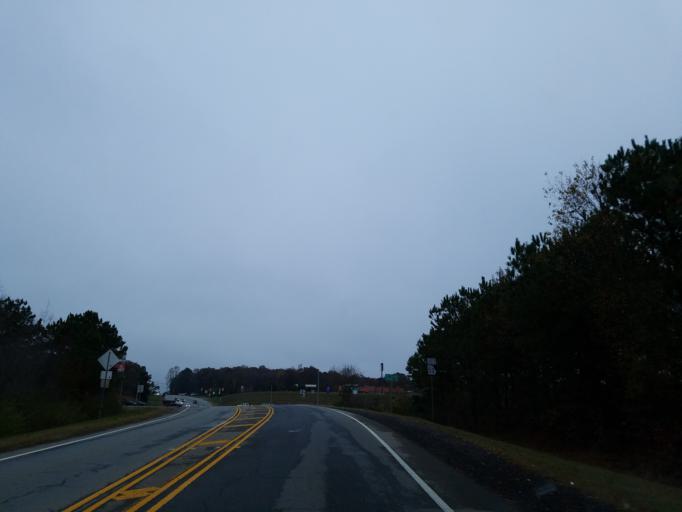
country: US
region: Georgia
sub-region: Pickens County
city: Nelson
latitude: 34.4053
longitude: -84.4238
